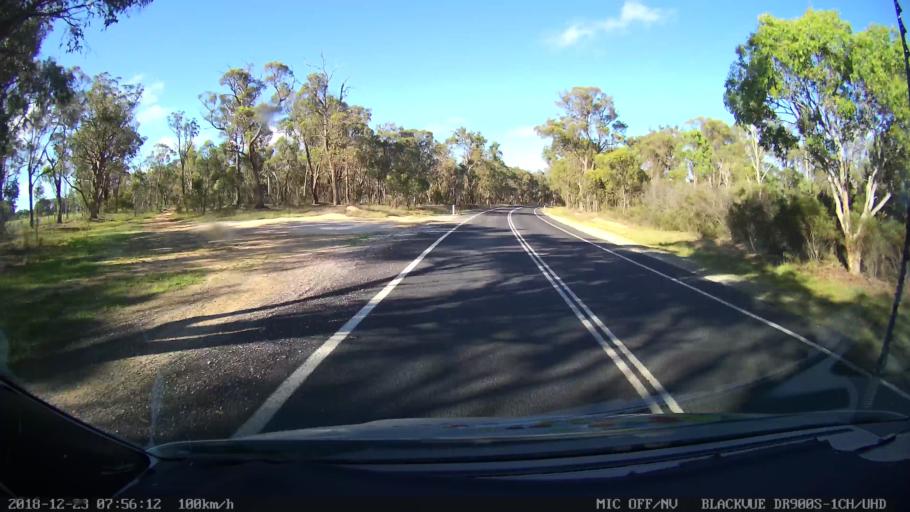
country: AU
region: New South Wales
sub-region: Armidale Dumaresq
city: Armidale
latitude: -30.5460
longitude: 151.7699
